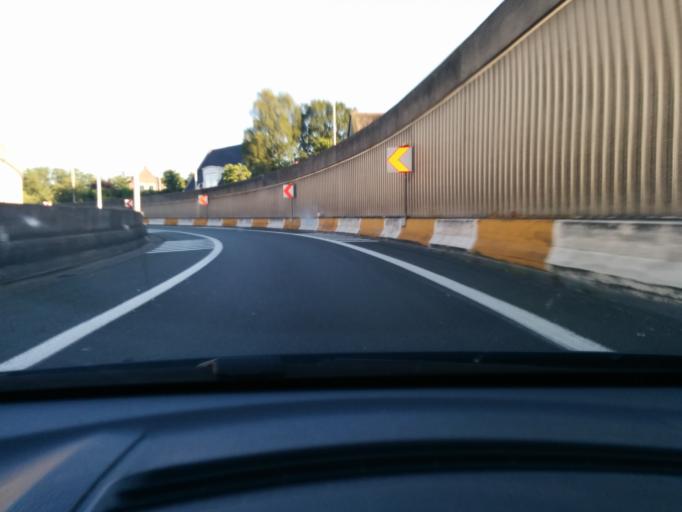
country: BE
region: Flanders
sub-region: Provincie Oost-Vlaanderen
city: De Pinte
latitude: 51.0195
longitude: 3.6834
